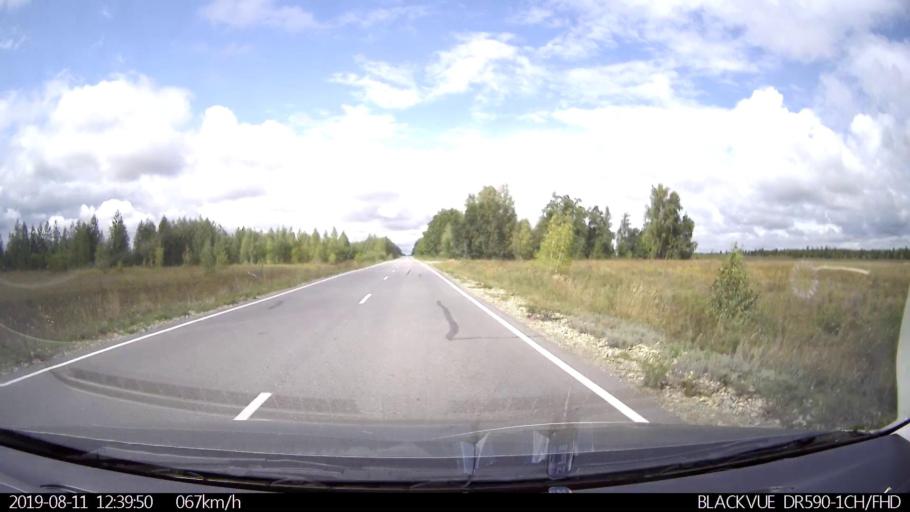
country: RU
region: Ulyanovsk
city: Ignatovka
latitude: 53.8353
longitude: 47.7897
